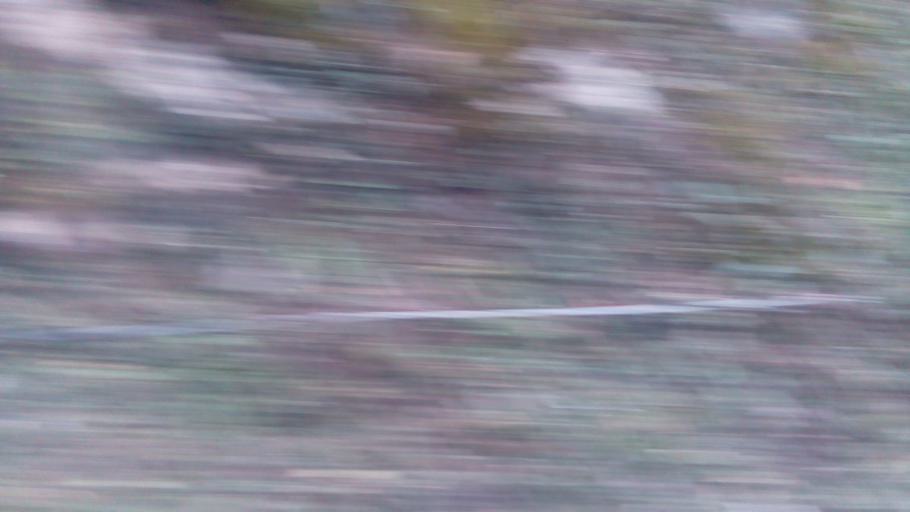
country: TW
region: Taiwan
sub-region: Yilan
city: Yilan
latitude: 24.5713
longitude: 121.4730
